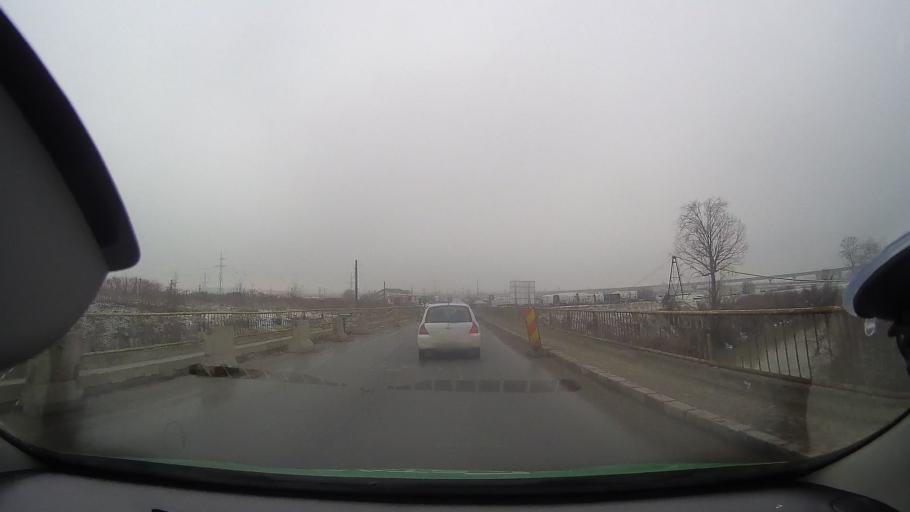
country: RO
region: Cluj
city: Turda
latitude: 46.5578
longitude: 23.7730
